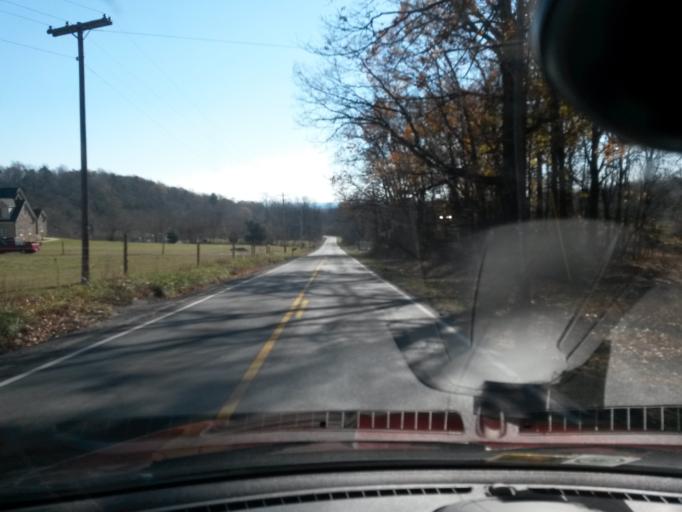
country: US
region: Virginia
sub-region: City of Bedford
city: Bedford
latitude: 37.4251
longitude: -79.5737
